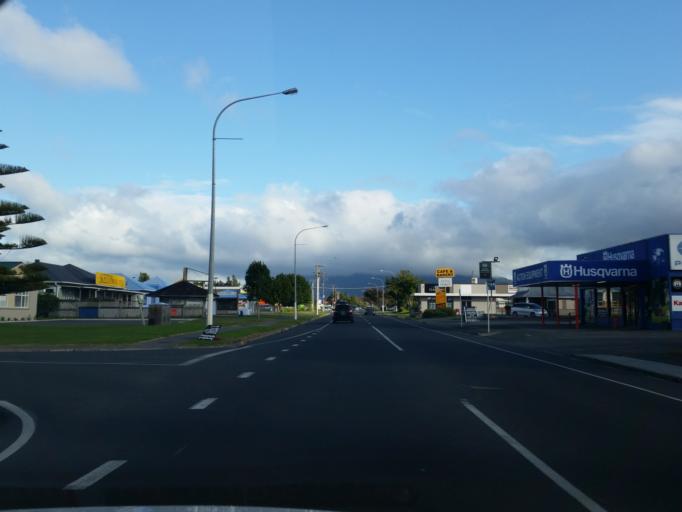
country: NZ
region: Bay of Plenty
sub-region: Western Bay of Plenty District
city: Katikati
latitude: -37.5576
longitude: 175.9166
